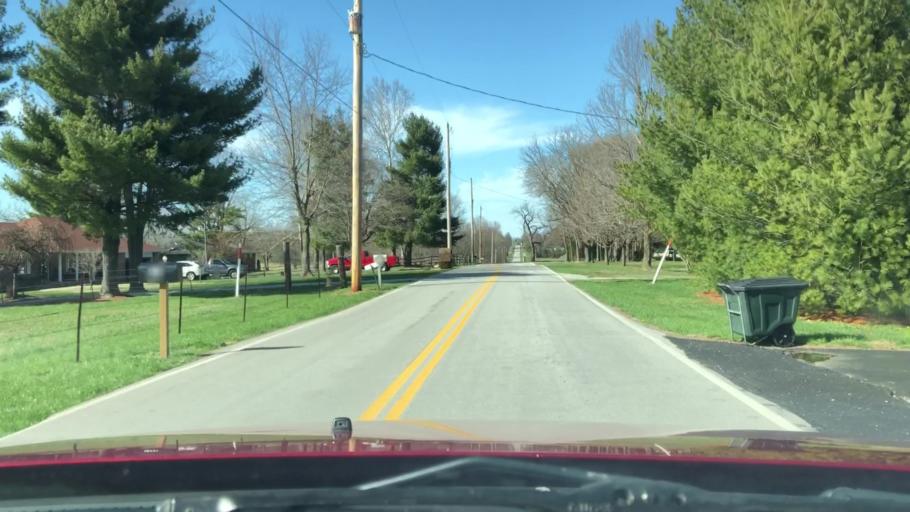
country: US
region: Missouri
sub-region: Greene County
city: Strafford
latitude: 37.2271
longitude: -93.1884
